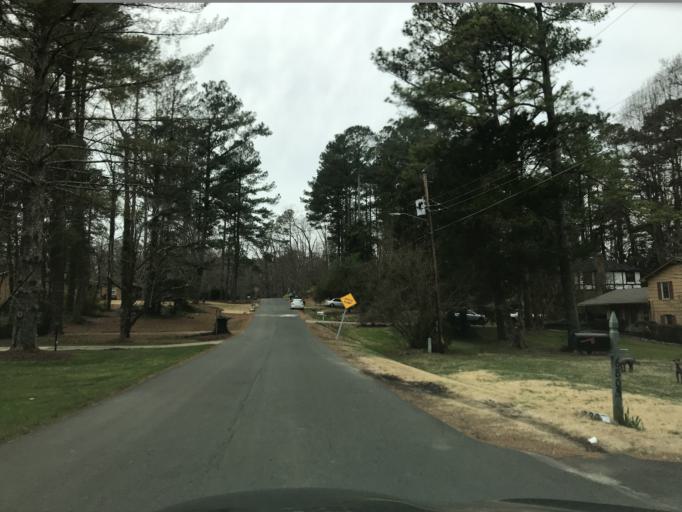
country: US
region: North Carolina
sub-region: Wake County
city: West Raleigh
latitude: 35.8726
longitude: -78.5977
